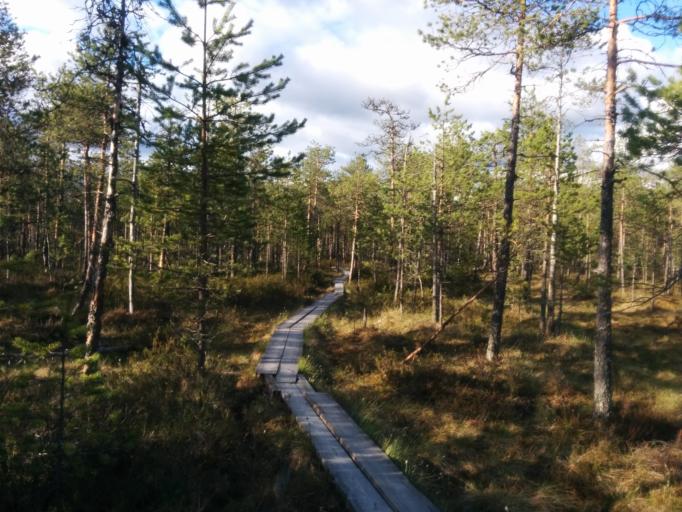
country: FI
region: Haeme
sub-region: Riihimaeki
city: Riihimaeki
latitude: 60.7588
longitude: 24.8243
